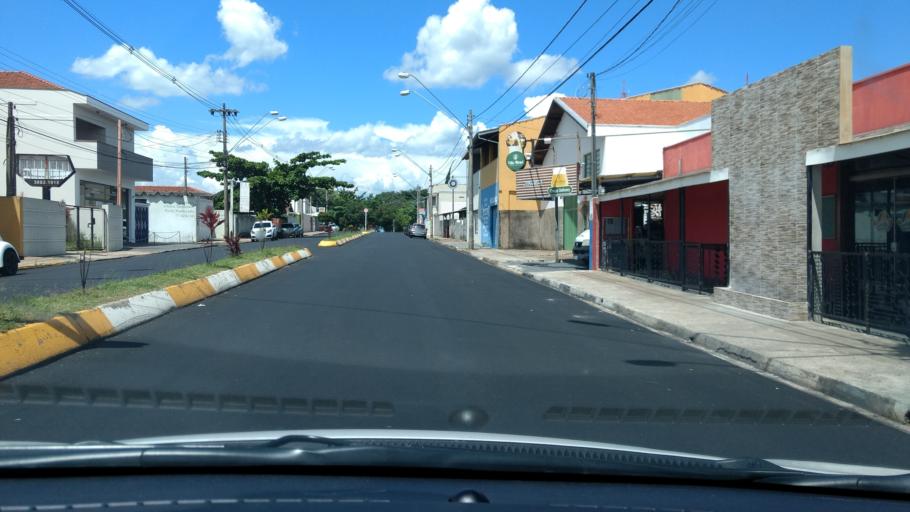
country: BR
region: Sao Paulo
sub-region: Botucatu
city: Botucatu
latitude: -22.8640
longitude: -48.4482
